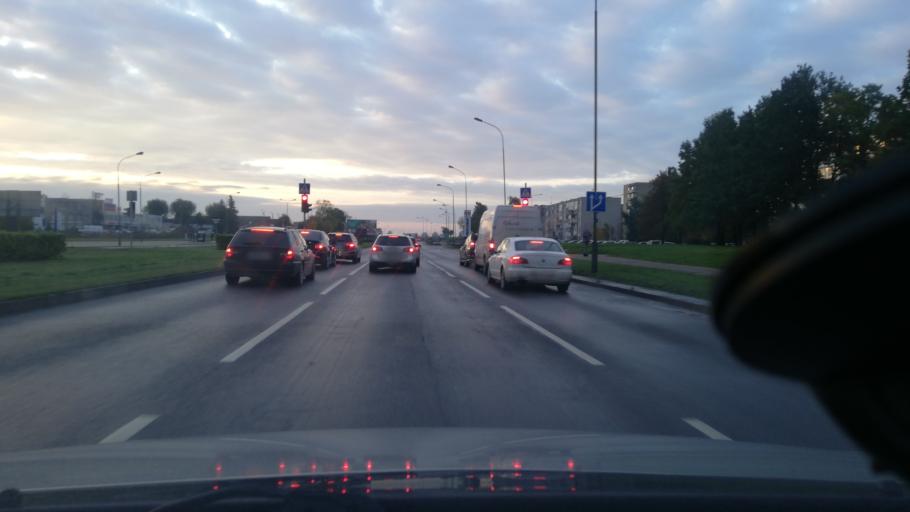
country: LT
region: Klaipedos apskritis
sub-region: Klaipeda
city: Klaipeda
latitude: 55.6903
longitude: 21.1798
